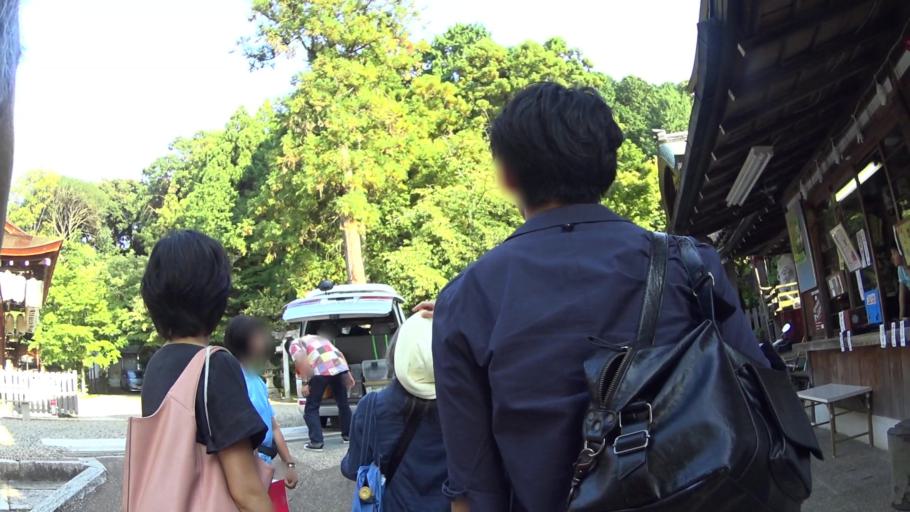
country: JP
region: Kyoto
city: Kyoto
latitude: 35.0082
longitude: 135.7849
